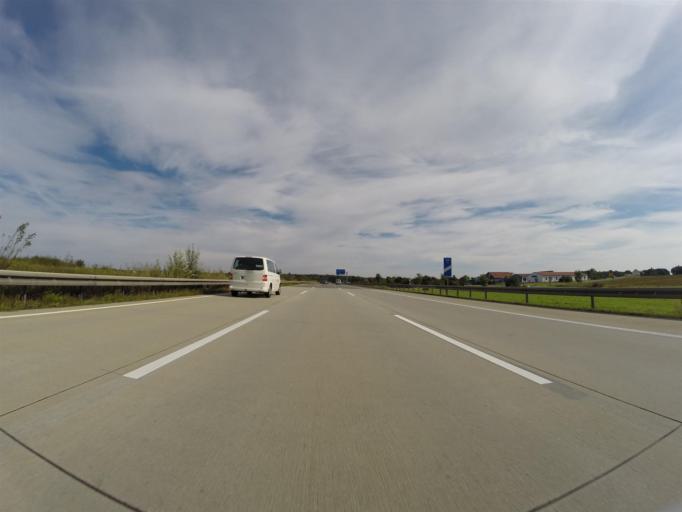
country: DE
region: Thuringia
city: Hermsdorf
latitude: 50.8888
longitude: 11.8738
